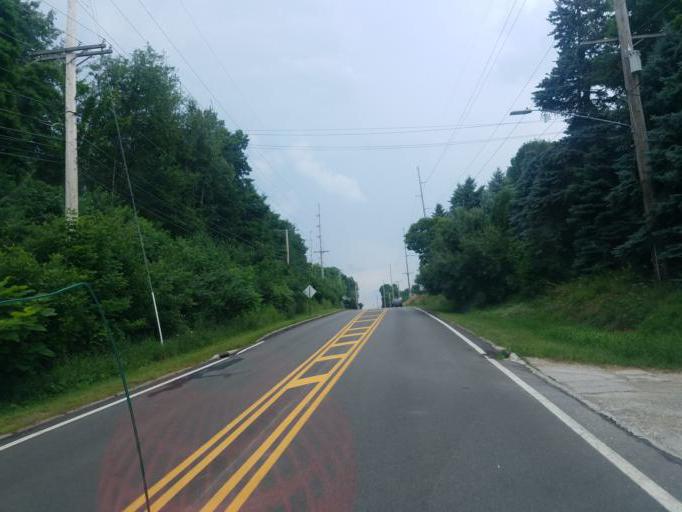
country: US
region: Ohio
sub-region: Medina County
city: Wadsworth
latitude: 41.0392
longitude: -81.7184
